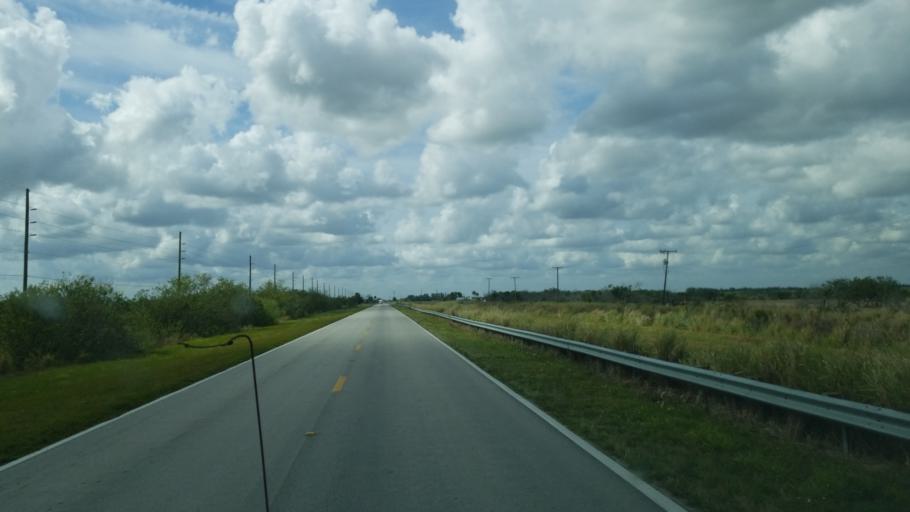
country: US
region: Florida
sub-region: Saint Lucie County
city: Lakewood Park
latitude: 27.4476
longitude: -80.5104
